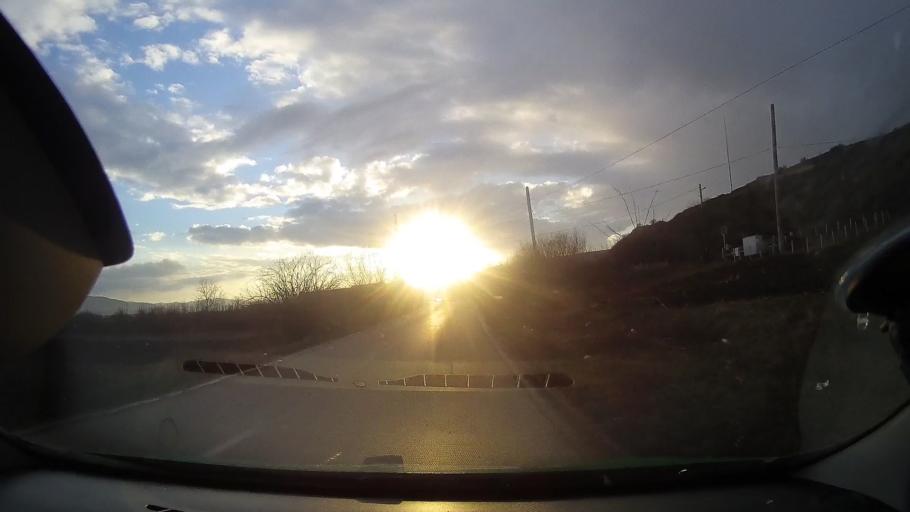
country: RO
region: Alba
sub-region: Oras Ocna Mures
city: Razboieni-Cetate
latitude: 46.4226
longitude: 23.8799
